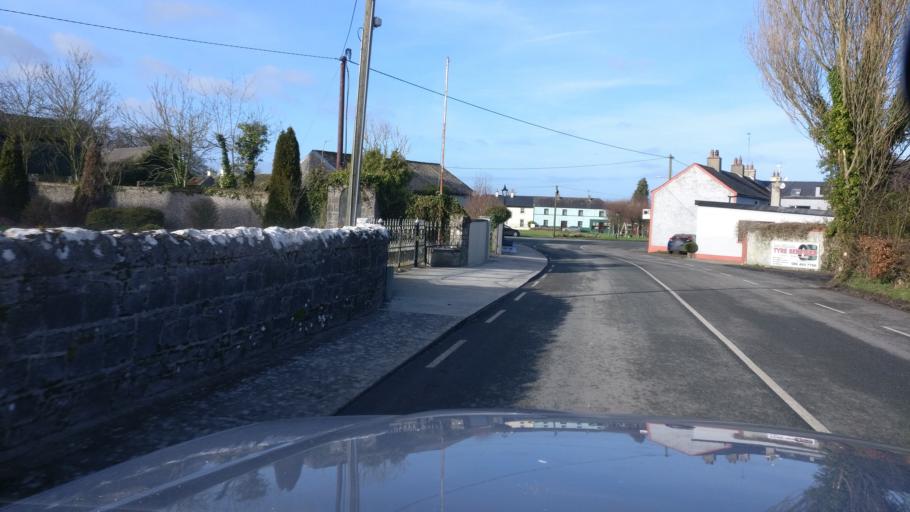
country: IE
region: Leinster
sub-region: Laois
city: Stradbally
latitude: 52.9599
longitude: -7.2011
